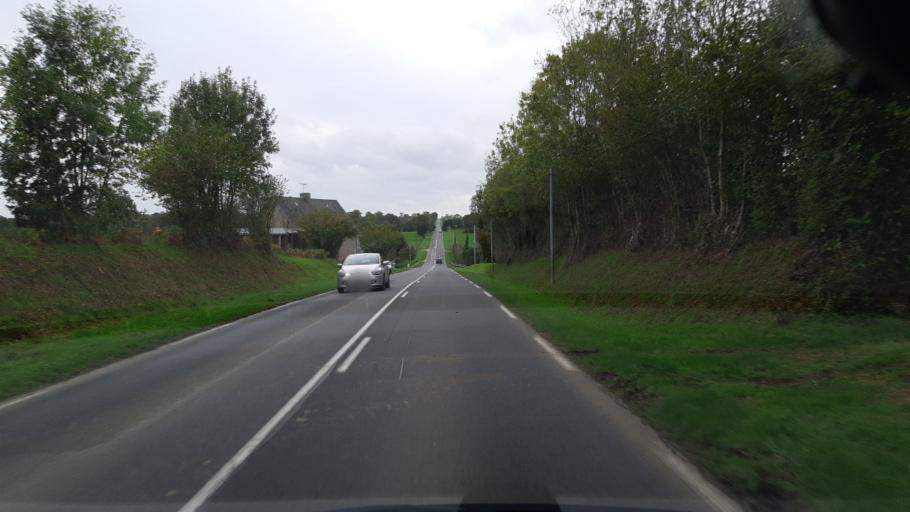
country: FR
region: Lower Normandy
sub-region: Departement de la Manche
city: Gavray
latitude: 48.9385
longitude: -1.3430
